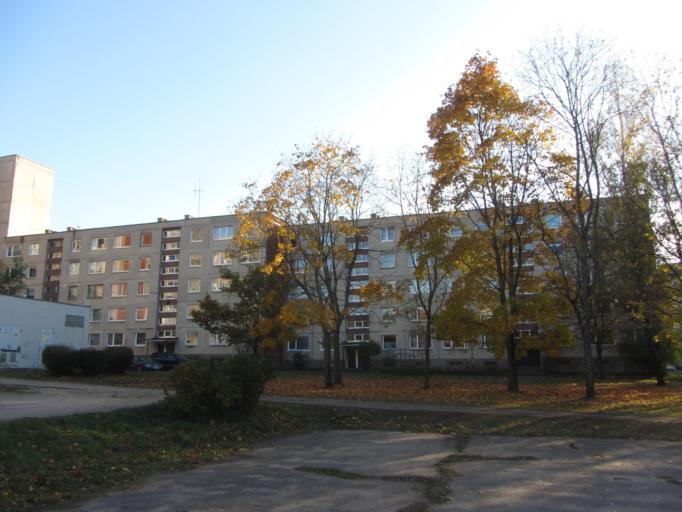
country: LT
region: Vilnius County
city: Lazdynai
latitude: 54.6871
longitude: 25.2025
